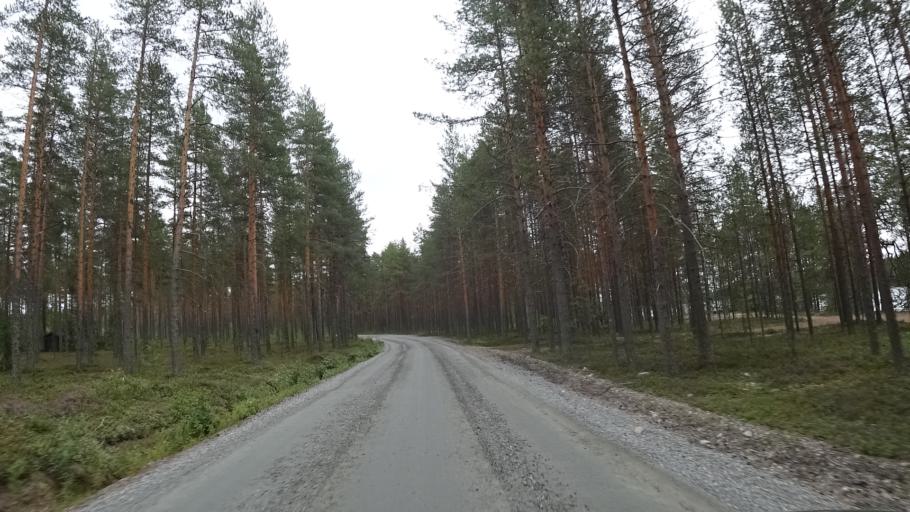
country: FI
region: North Karelia
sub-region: Pielisen Karjala
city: Lieksa
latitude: 63.3787
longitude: 30.3455
